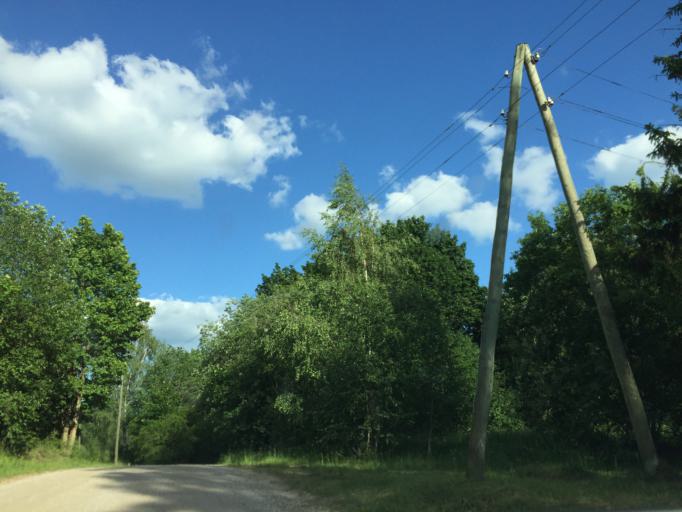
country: LV
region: Kandava
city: Kandava
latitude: 56.8363
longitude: 22.7450
